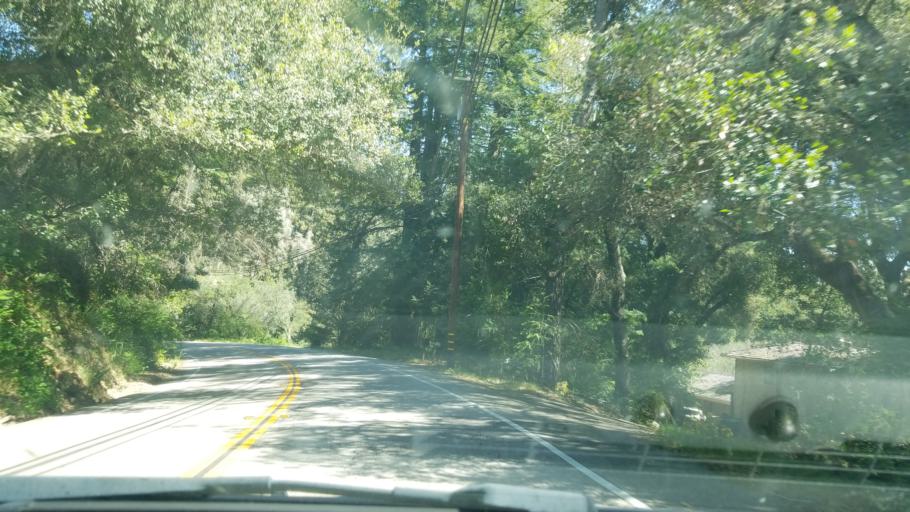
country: US
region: California
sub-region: Santa Clara County
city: Lexington Hills
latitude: 37.1096
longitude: -121.9477
